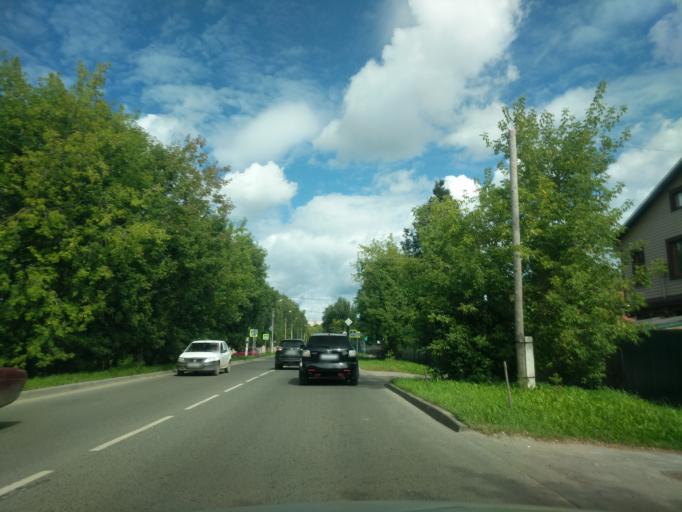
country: RU
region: Kostroma
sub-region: Kostromskoy Rayon
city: Kostroma
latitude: 57.7761
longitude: 40.9527
